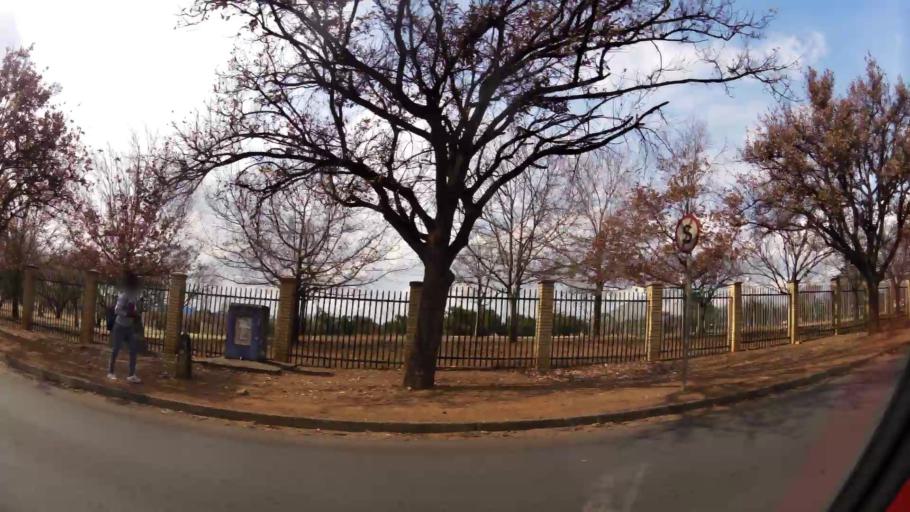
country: ZA
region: Gauteng
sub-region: Sedibeng District Municipality
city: Vanderbijlpark
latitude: -26.7153
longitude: 27.8630
